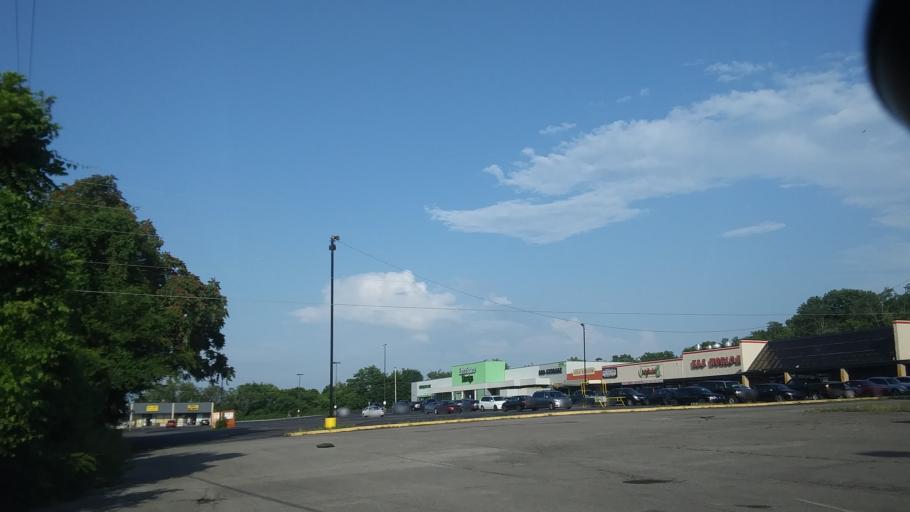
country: US
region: Tennessee
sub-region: Davidson County
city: Belle Meade
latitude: 36.1477
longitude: -86.8647
